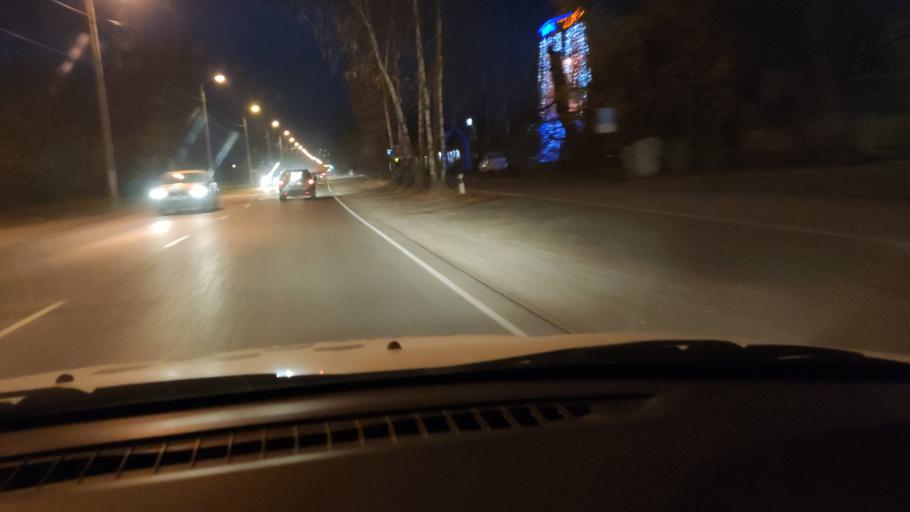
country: RU
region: Perm
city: Kondratovo
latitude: 57.9762
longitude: 56.1295
